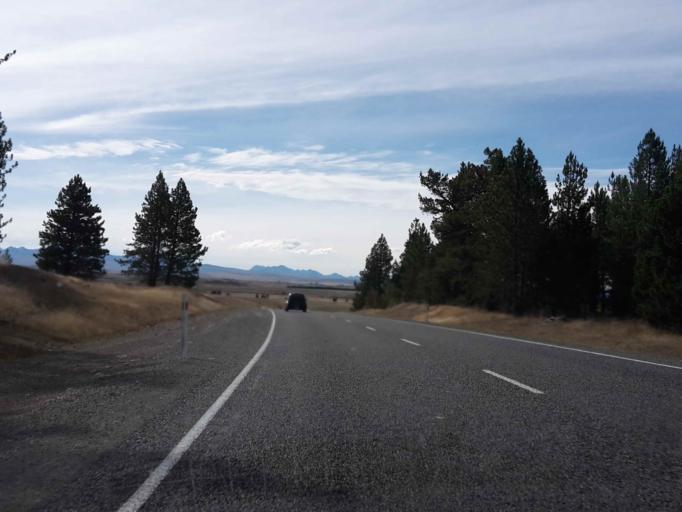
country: NZ
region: Canterbury
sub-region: Timaru District
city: Pleasant Point
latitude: -44.1789
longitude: 170.3195
